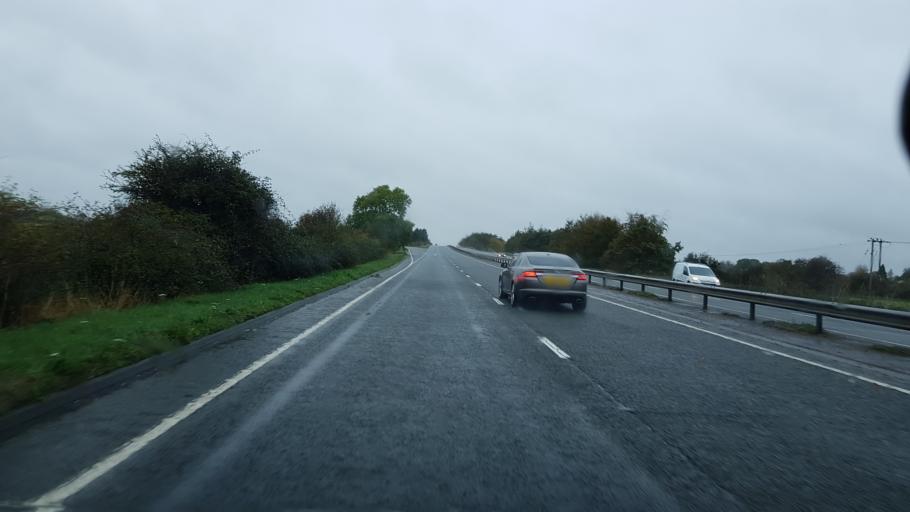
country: GB
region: England
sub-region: Oxfordshire
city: Carterton
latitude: 51.7818
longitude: -1.5463
